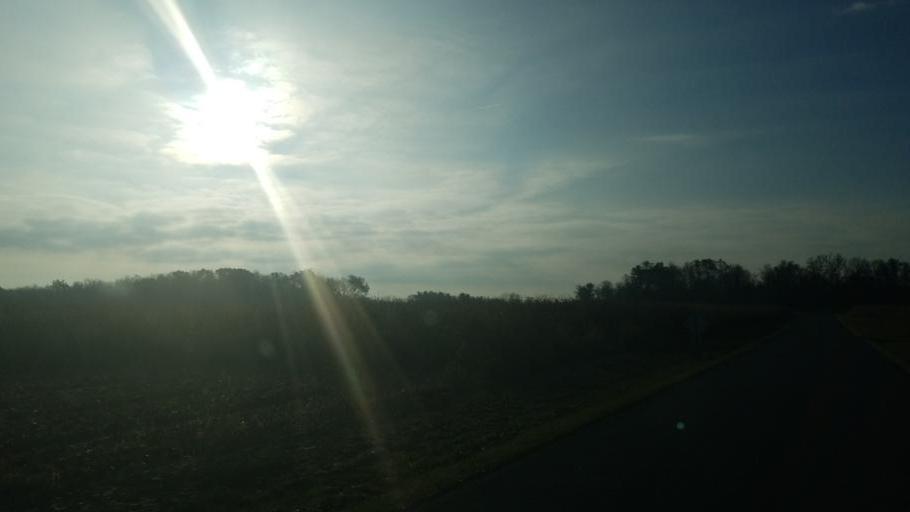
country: US
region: Ohio
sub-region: Morrow County
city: Mount Gilead
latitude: 40.5360
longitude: -82.7953
